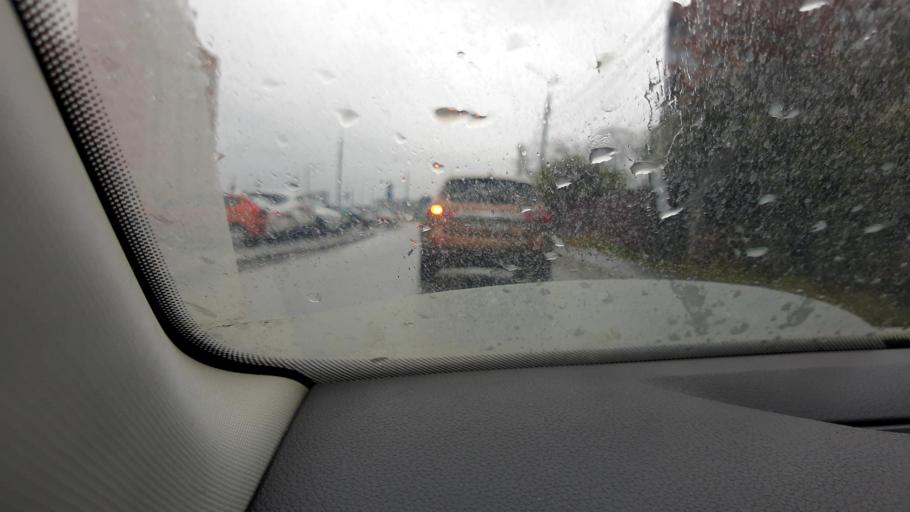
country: RU
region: Moskovskaya
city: Aprelevka
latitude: 55.5414
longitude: 37.0765
